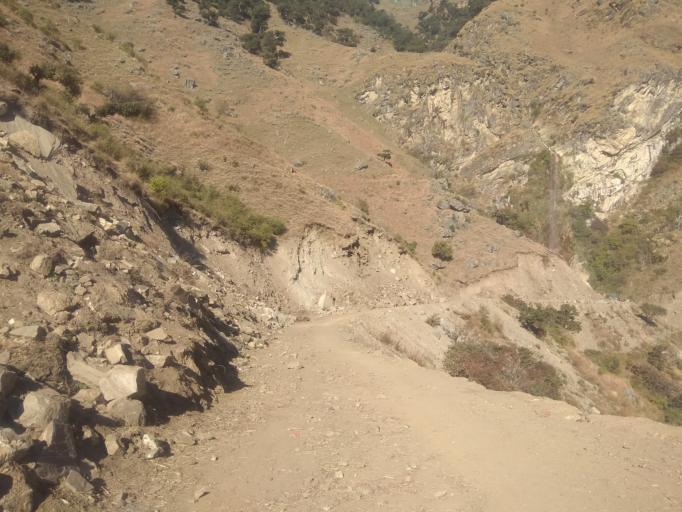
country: NP
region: Mid Western
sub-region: Bheri Zone
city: Dailekh
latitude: 29.2934
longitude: 81.7080
